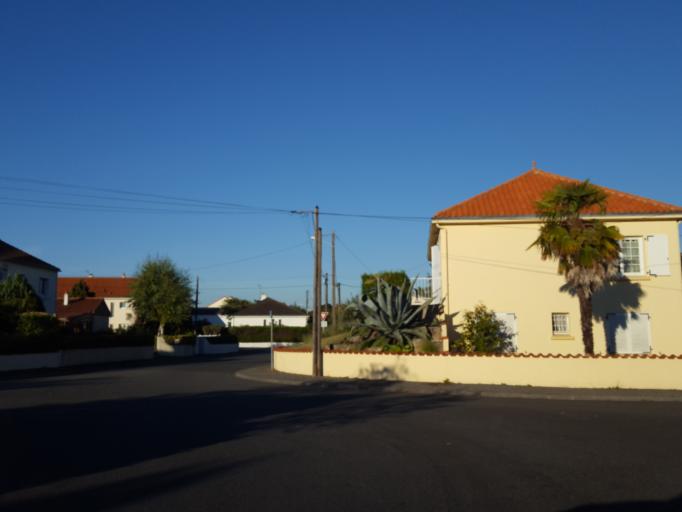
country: FR
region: Pays de la Loire
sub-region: Departement de la Loire-Atlantique
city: Basse-Goulaine
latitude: 47.2111
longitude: -1.4690
